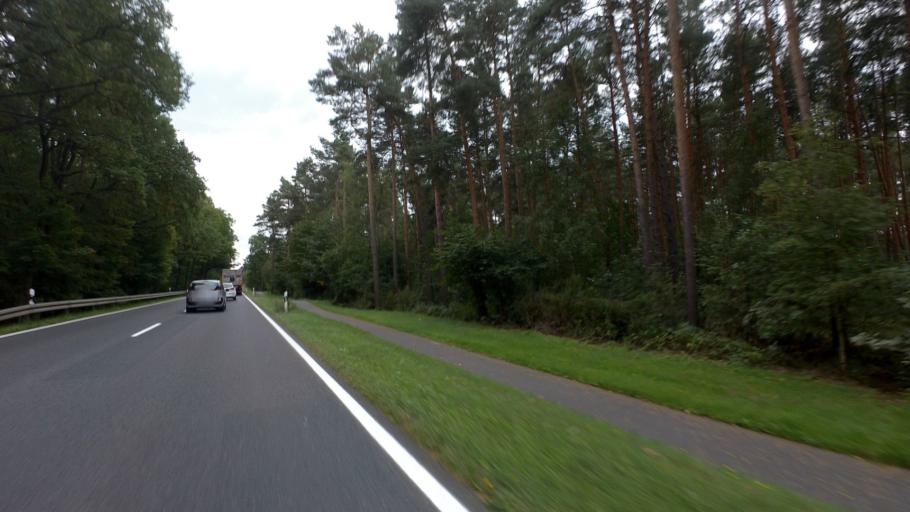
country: DE
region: Saxony
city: Neschwitz
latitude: 51.2868
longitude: 14.3313
